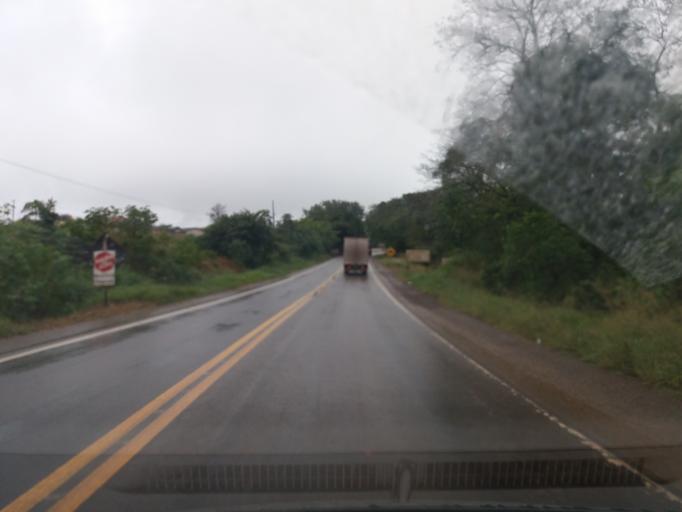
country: BR
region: Parana
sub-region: Realeza
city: Realeza
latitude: -25.4943
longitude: -53.5994
